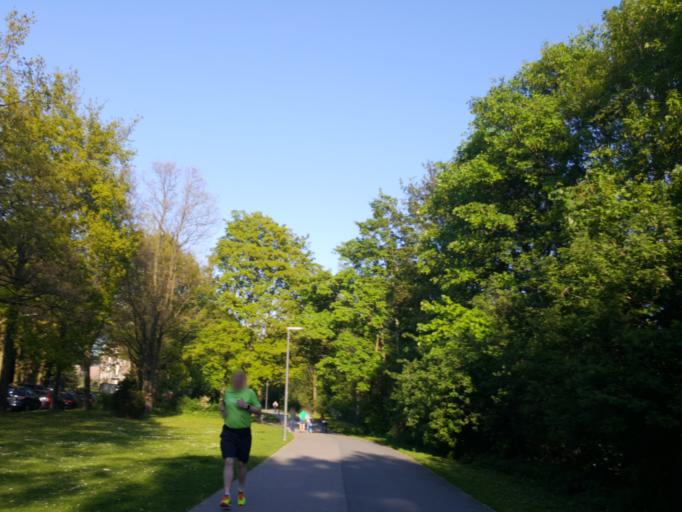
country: DE
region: Hamburg
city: Borgfelde
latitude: 53.5561
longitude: 10.0487
